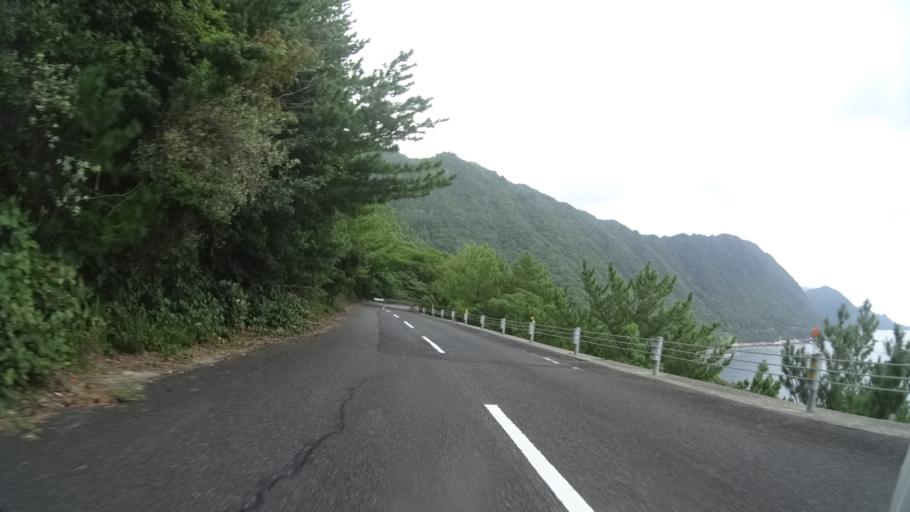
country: JP
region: Kagoshima
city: Nishinoomote
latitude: 30.3200
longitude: 130.3972
